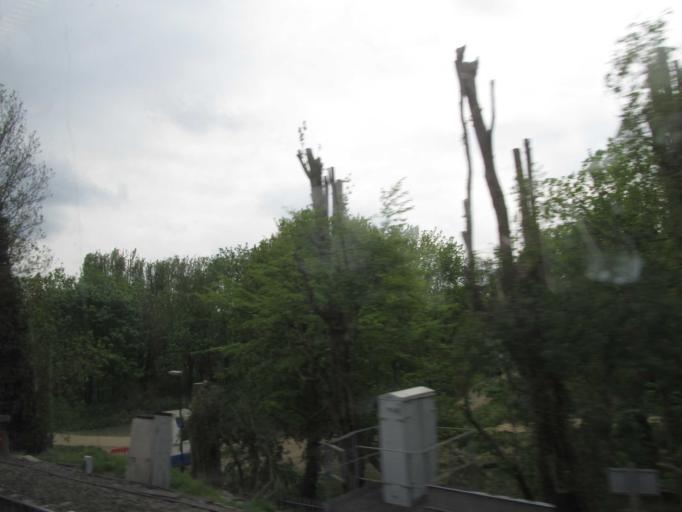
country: GB
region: England
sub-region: Slough
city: Slough
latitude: 51.5149
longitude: -0.6063
